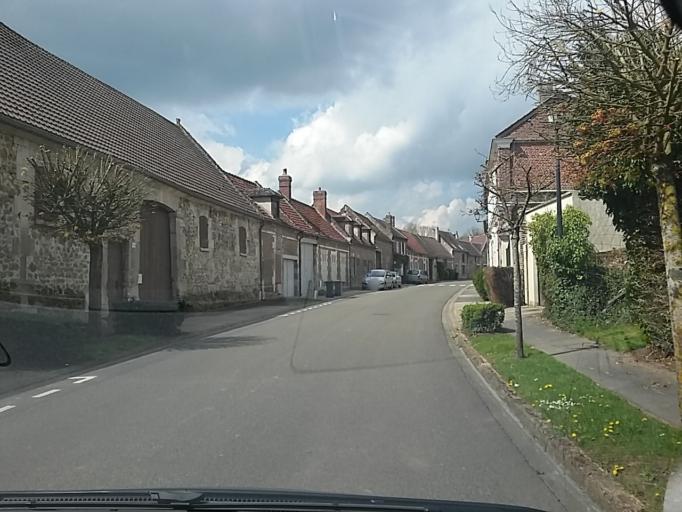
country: FR
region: Picardie
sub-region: Departement de l'Oise
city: Grandfresnoy
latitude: 49.3670
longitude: 2.6564
